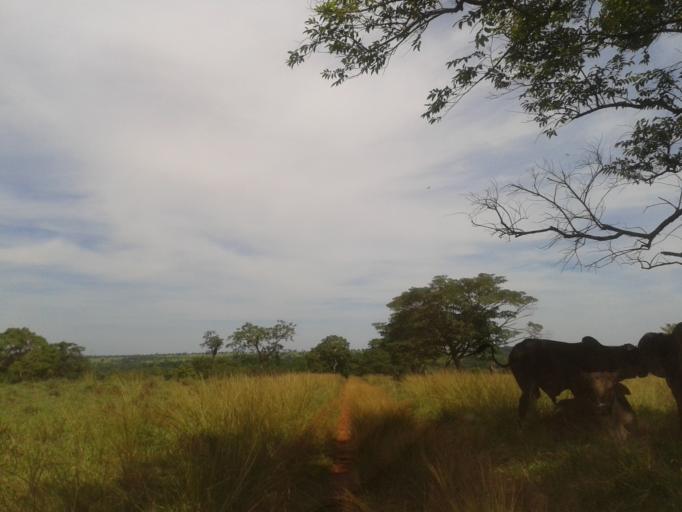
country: BR
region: Minas Gerais
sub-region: Santa Vitoria
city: Santa Vitoria
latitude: -19.1286
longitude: -50.5515
